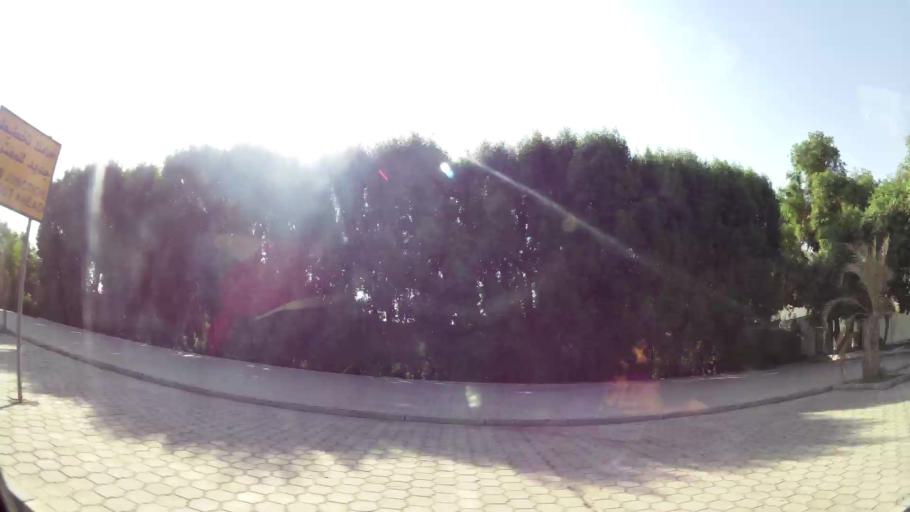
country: KW
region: Al Asimah
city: Ash Shamiyah
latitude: 29.3555
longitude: 47.9464
